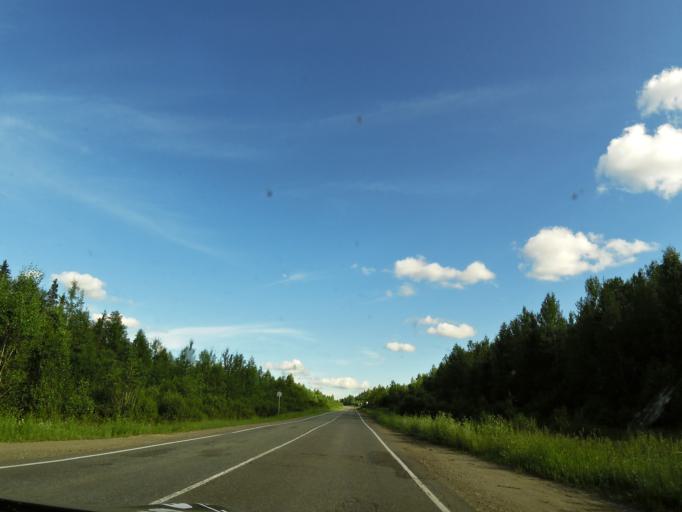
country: RU
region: Kirov
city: Omutninsk
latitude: 58.7259
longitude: 52.0813
